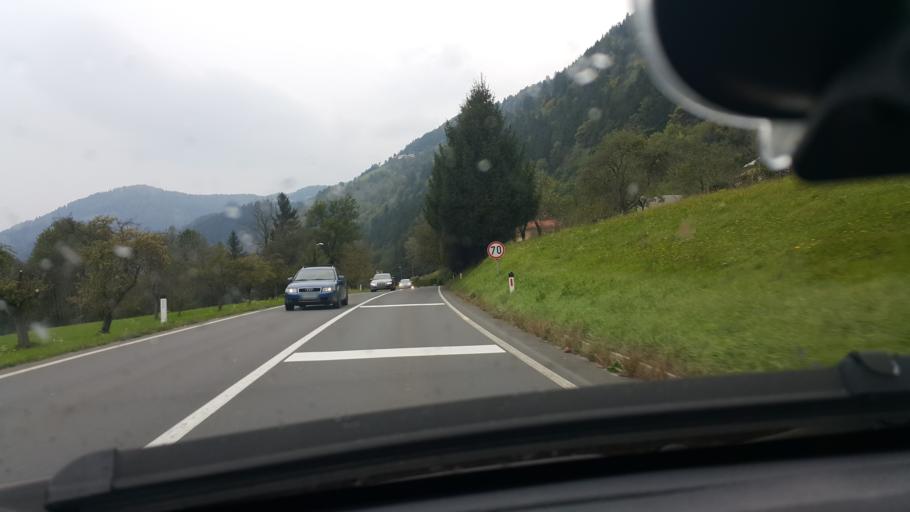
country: SI
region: Dravograd
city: Dravograd
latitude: 46.6043
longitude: 15.0828
